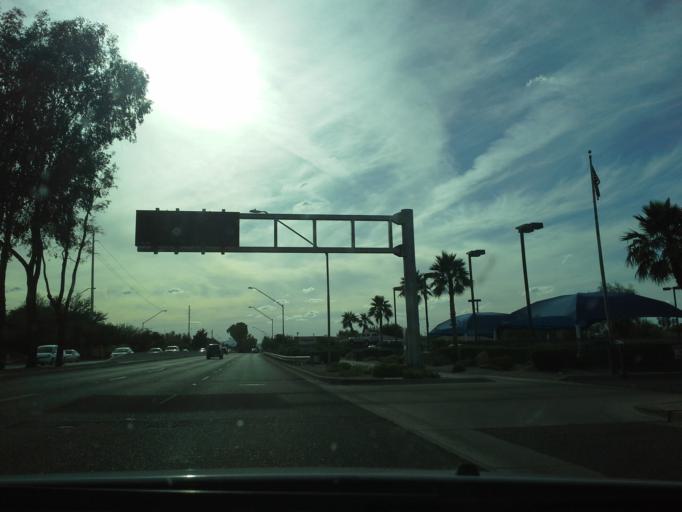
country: US
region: Arizona
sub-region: Maricopa County
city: Peoria
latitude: 33.6384
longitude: -112.2110
